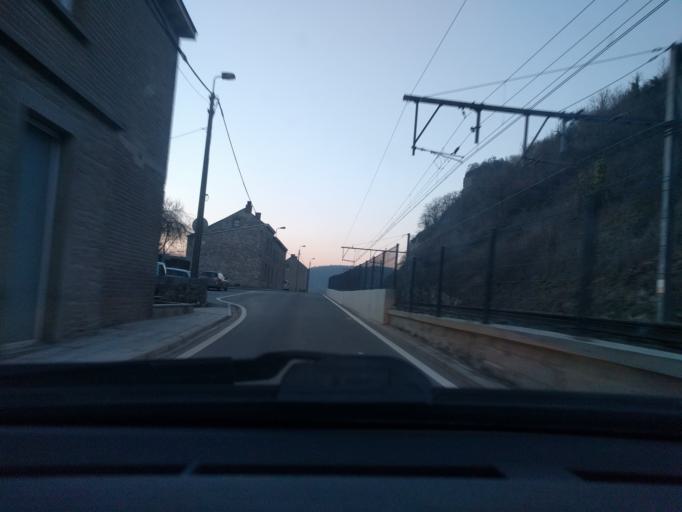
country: BE
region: Wallonia
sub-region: Province de Namur
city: Noville-les-Bois
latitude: 50.4717
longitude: 4.9864
